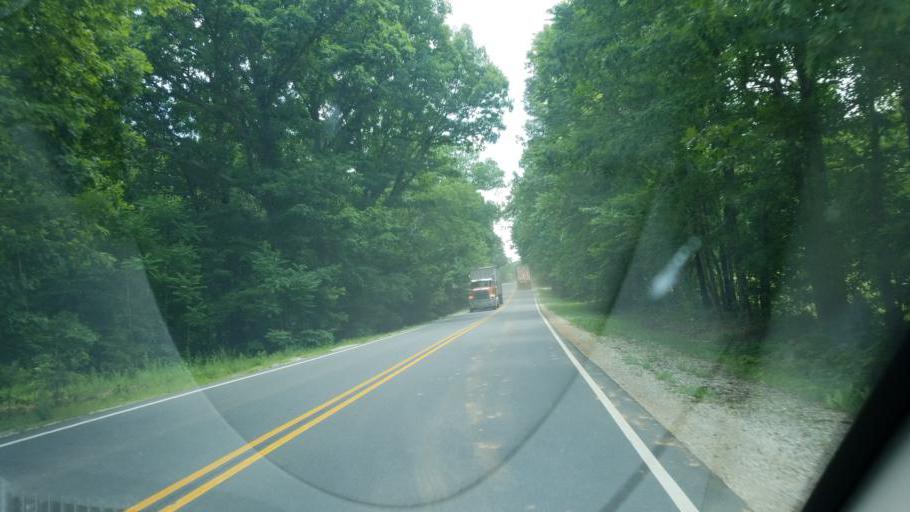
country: US
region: Virginia
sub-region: Amherst County
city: Amherst
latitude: 37.5742
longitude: -78.8834
